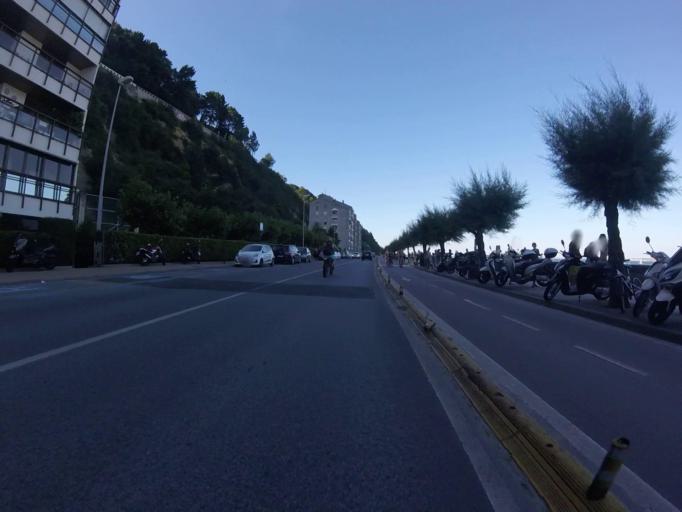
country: ES
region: Basque Country
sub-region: Provincia de Guipuzcoa
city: Fuenterrabia
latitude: 43.3820
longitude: -1.7975
